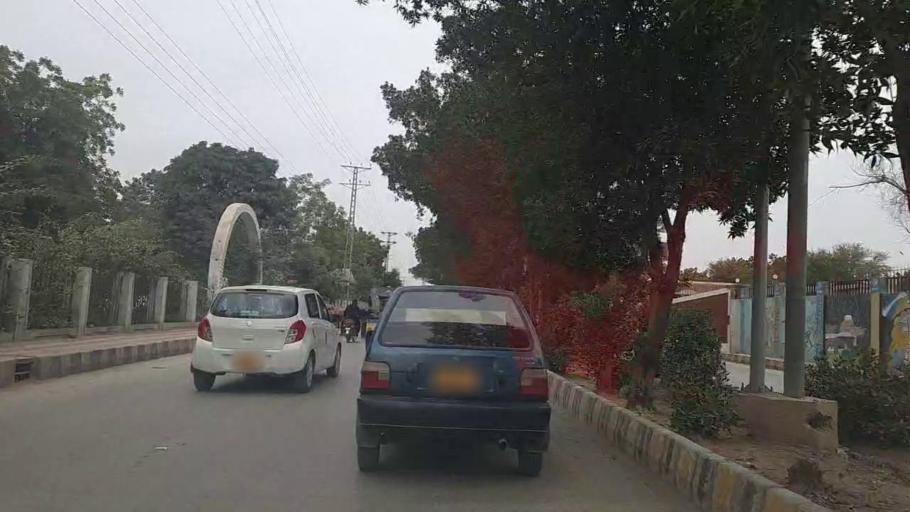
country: PK
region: Sindh
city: Nawabshah
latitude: 26.2477
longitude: 68.4018
